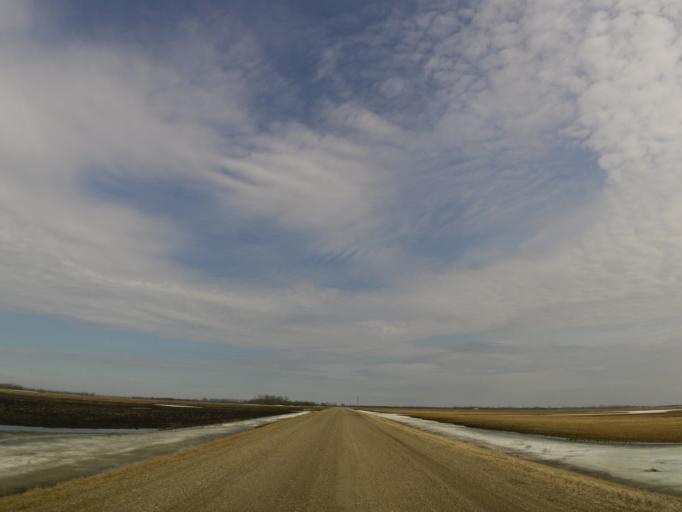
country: US
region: North Dakota
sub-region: Walsh County
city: Grafton
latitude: 48.4266
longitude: -97.2177
